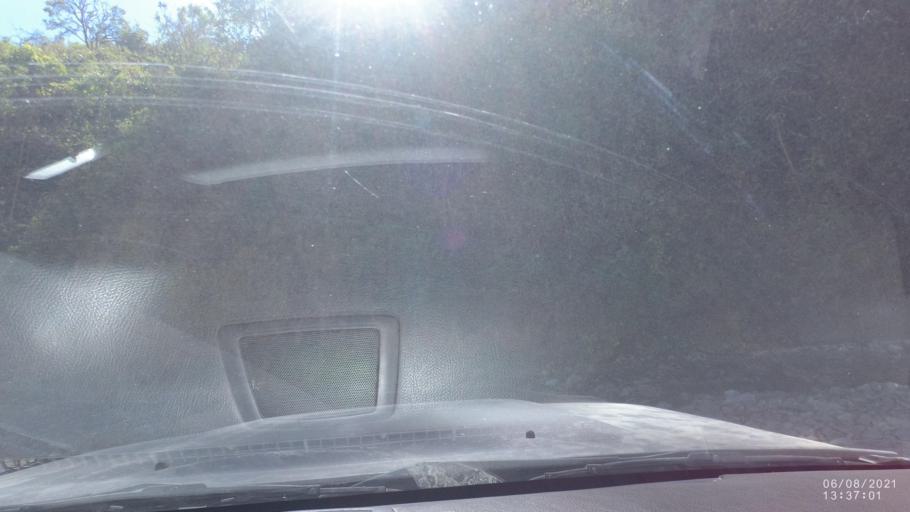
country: BO
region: La Paz
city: Quime
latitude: -16.6899
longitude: -66.7215
